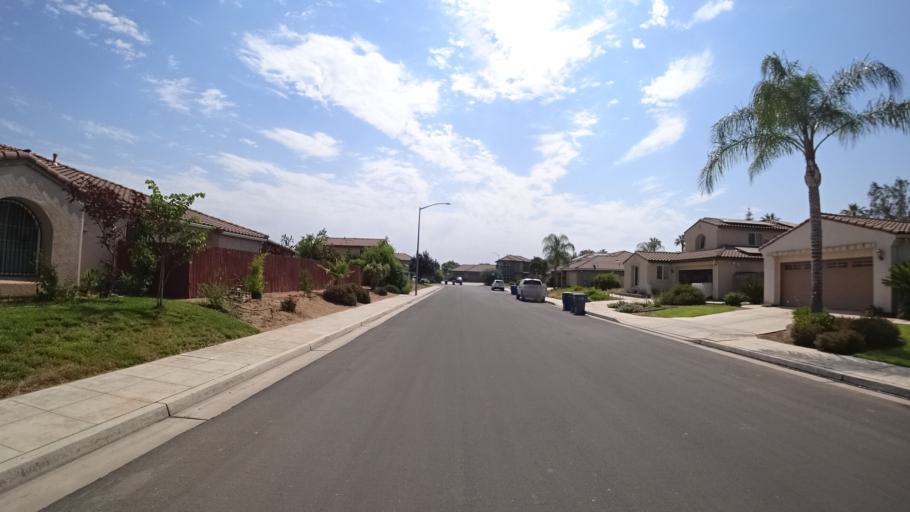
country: US
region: California
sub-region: Fresno County
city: West Park
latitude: 36.7290
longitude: -119.8460
